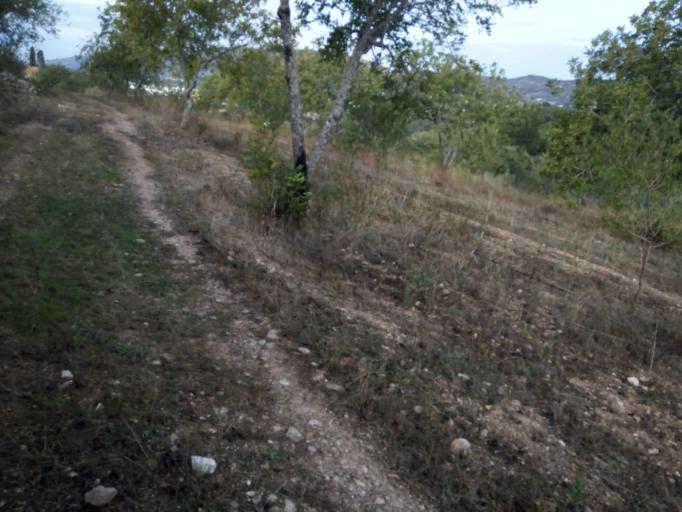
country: PT
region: Faro
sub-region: Faro
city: Santa Barbara de Nexe
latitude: 37.1020
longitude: -7.9564
